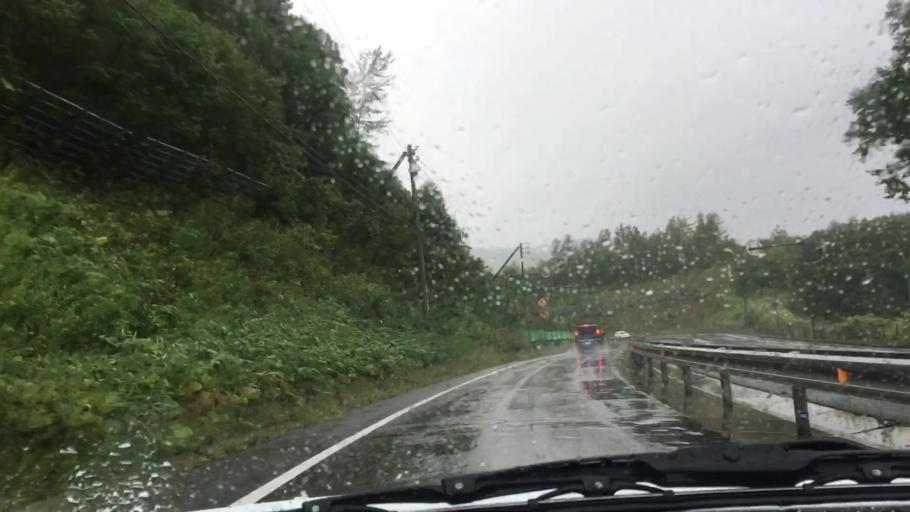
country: JP
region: Hokkaido
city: Otaru
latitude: 42.8501
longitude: 141.0684
